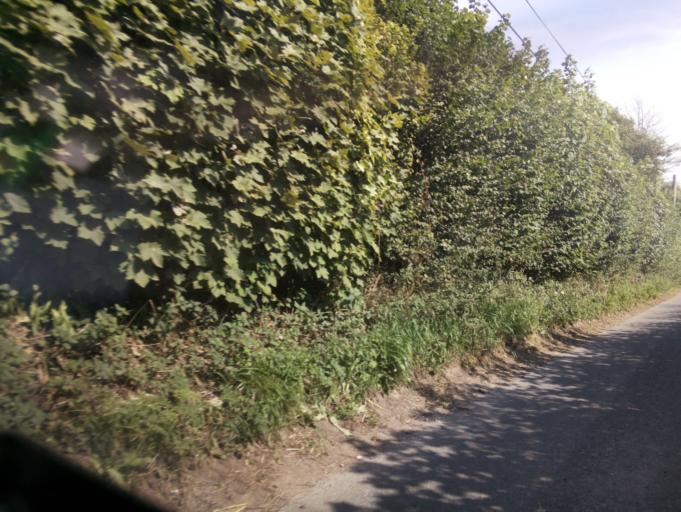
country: GB
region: England
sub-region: Gloucestershire
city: Dursley
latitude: 51.6861
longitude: -2.3198
